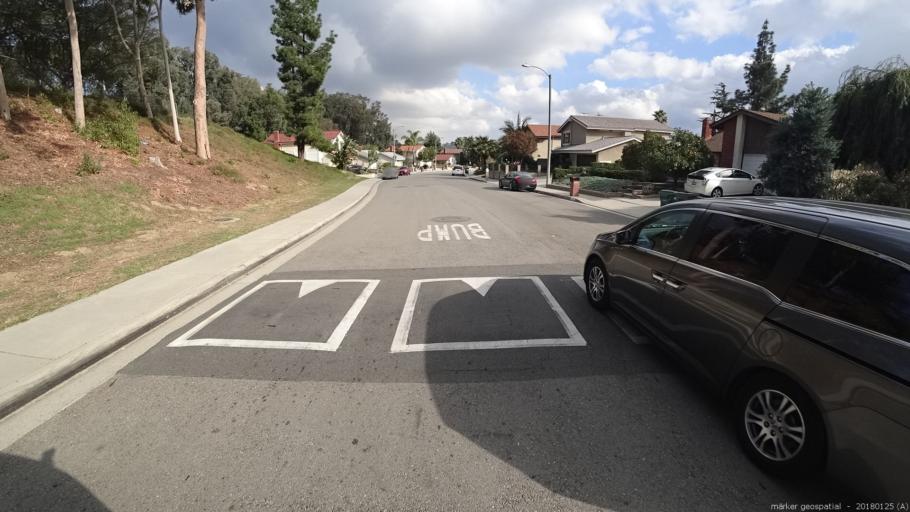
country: US
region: California
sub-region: Los Angeles County
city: Diamond Bar
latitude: 33.9956
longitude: -117.8246
